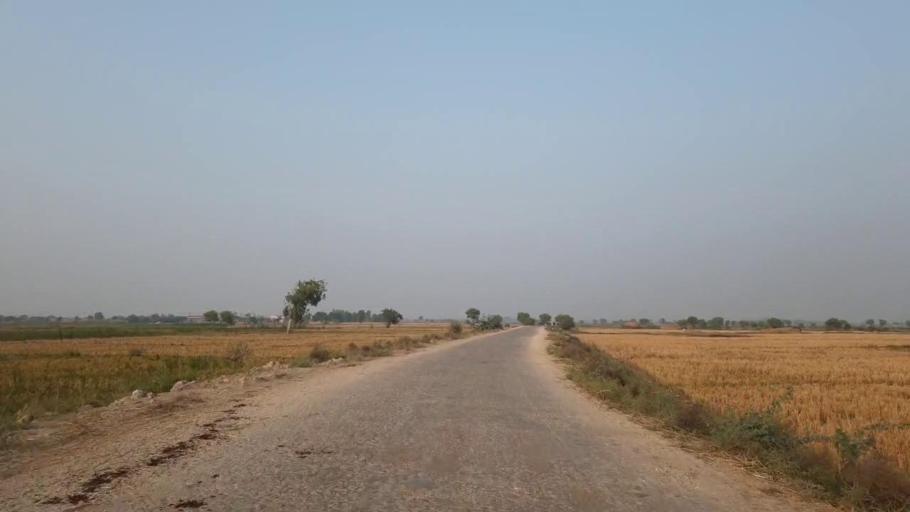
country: PK
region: Sindh
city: Tando Muhammad Khan
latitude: 25.0870
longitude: 68.4334
